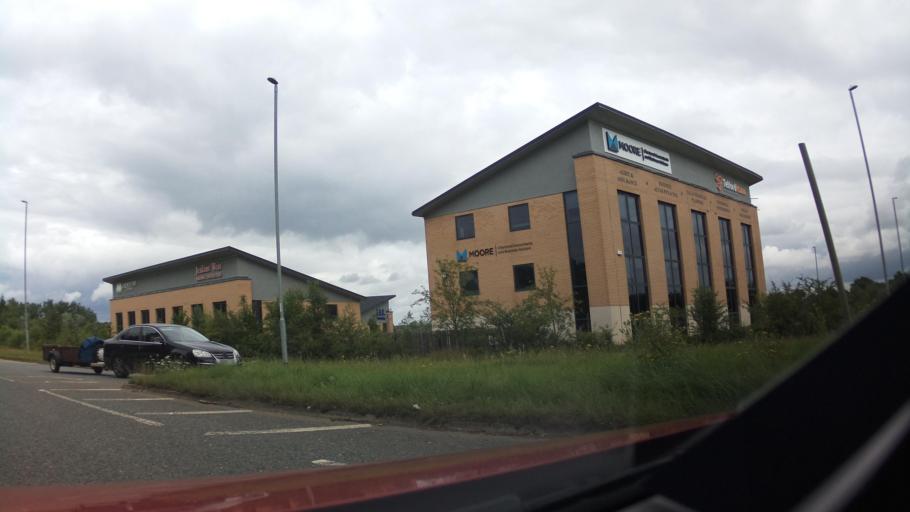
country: GB
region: England
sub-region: Northamptonshire
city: Geddington
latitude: 52.4600
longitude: -0.7375
